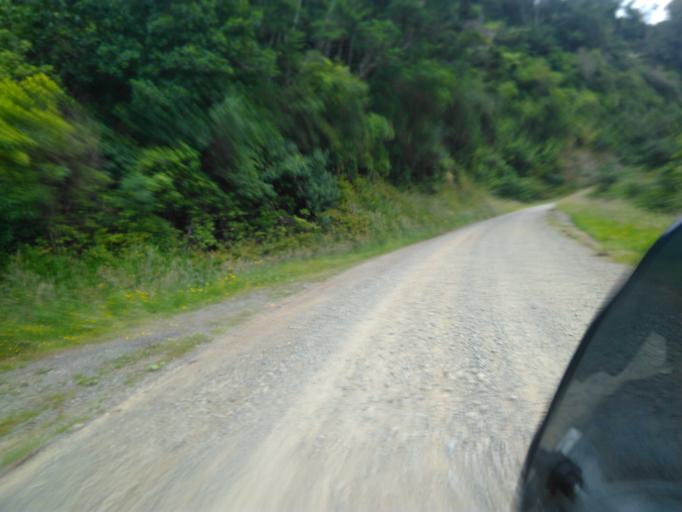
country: NZ
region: Bay of Plenty
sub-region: Opotiki District
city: Opotiki
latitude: -38.0362
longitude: 177.4412
